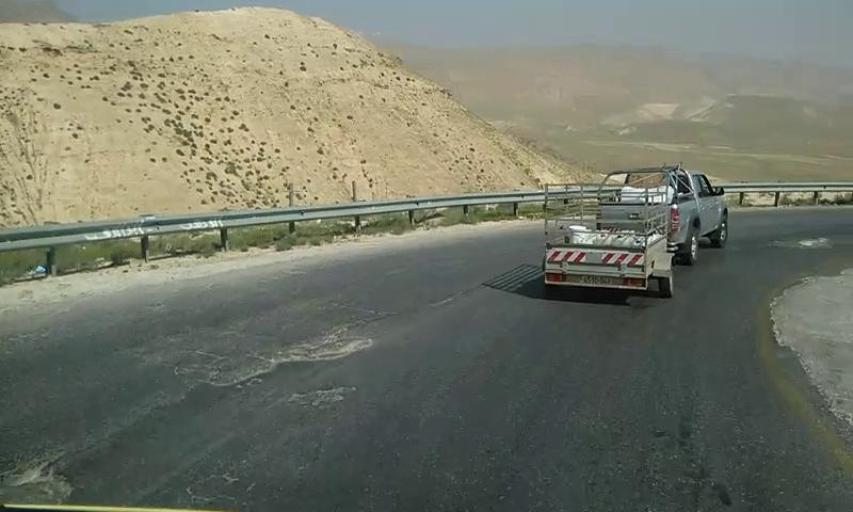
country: PS
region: West Bank
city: An Nuway`imah
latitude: 31.9135
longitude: 35.3833
